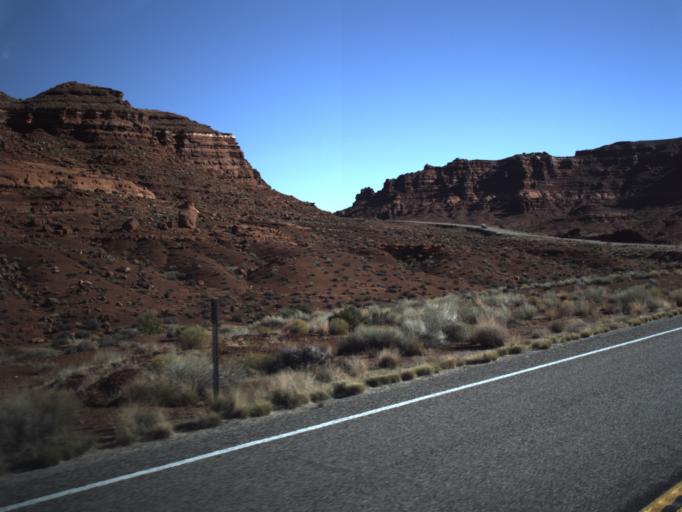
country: US
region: Utah
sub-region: San Juan County
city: Blanding
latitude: 37.8612
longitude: -110.3507
